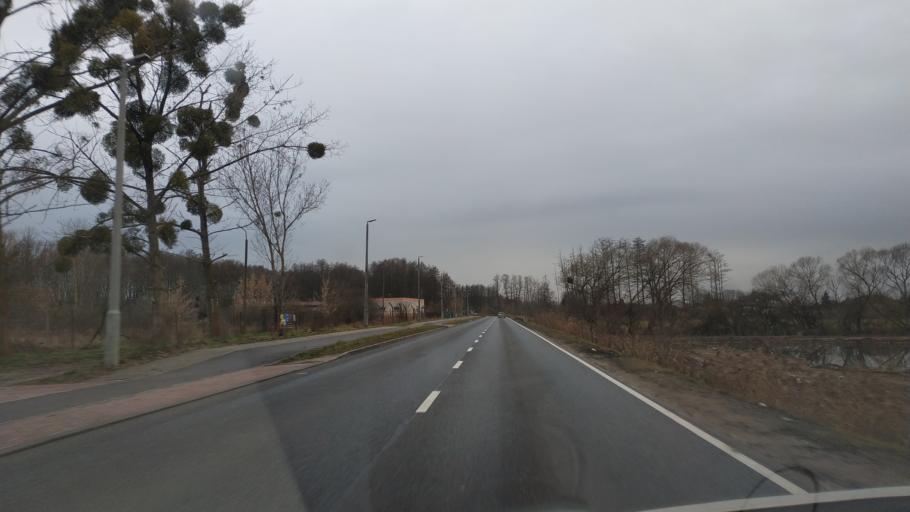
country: PL
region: Kujawsko-Pomorskie
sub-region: Torun
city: Torun
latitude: 52.9948
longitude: 18.5828
